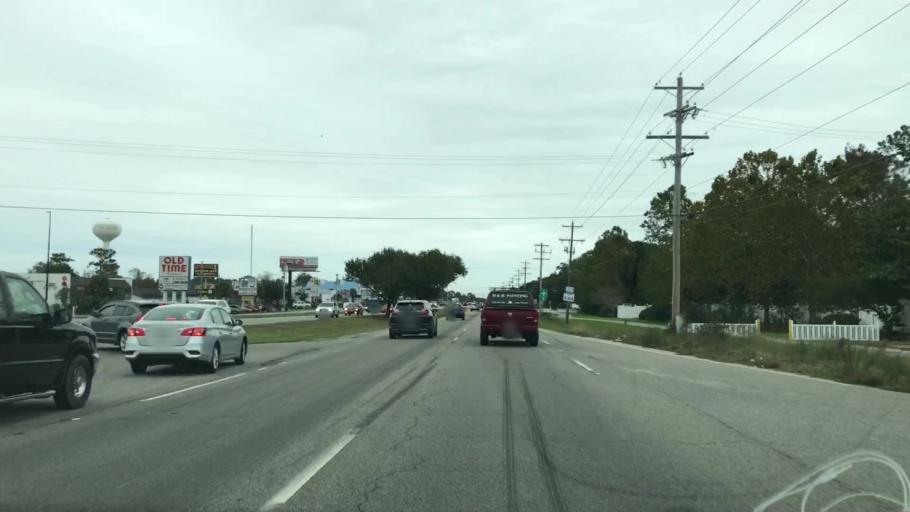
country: US
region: South Carolina
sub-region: Horry County
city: Surfside Beach
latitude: 33.6257
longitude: -78.9668
